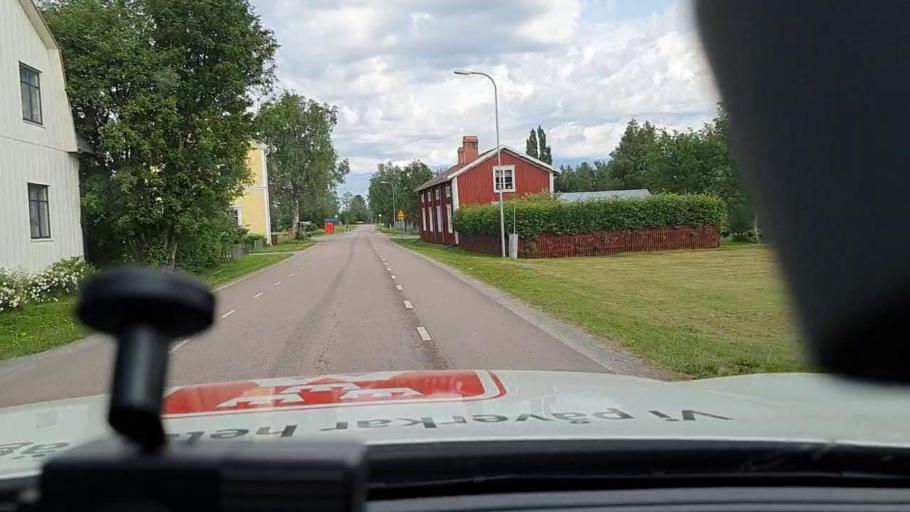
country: SE
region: Norrbotten
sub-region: Bodens Kommun
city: Saevast
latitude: 65.6817
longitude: 21.8011
